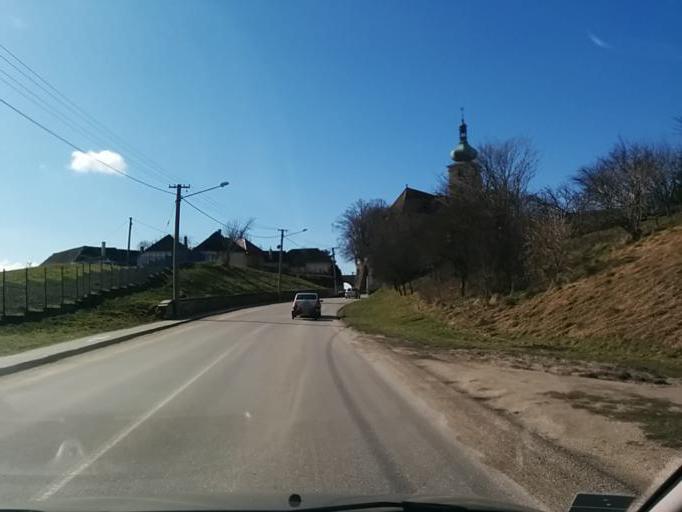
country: SK
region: Nitriansky
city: Cachtice
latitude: 48.7167
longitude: 17.7883
